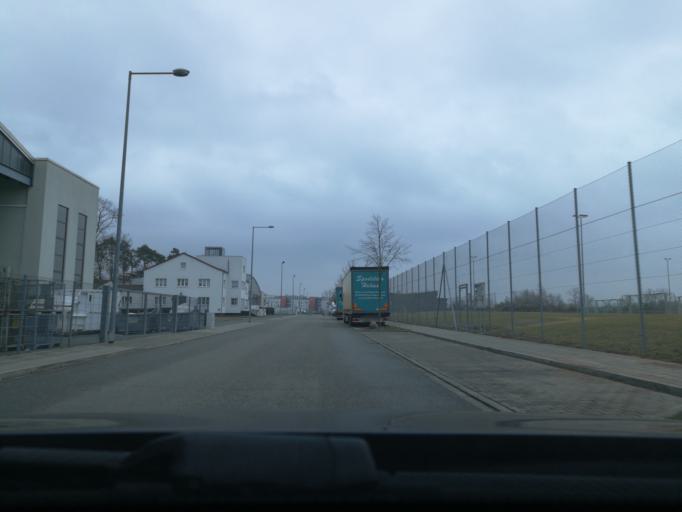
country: DE
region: Bavaria
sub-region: Regierungsbezirk Mittelfranken
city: Furth
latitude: 49.5032
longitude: 10.9637
